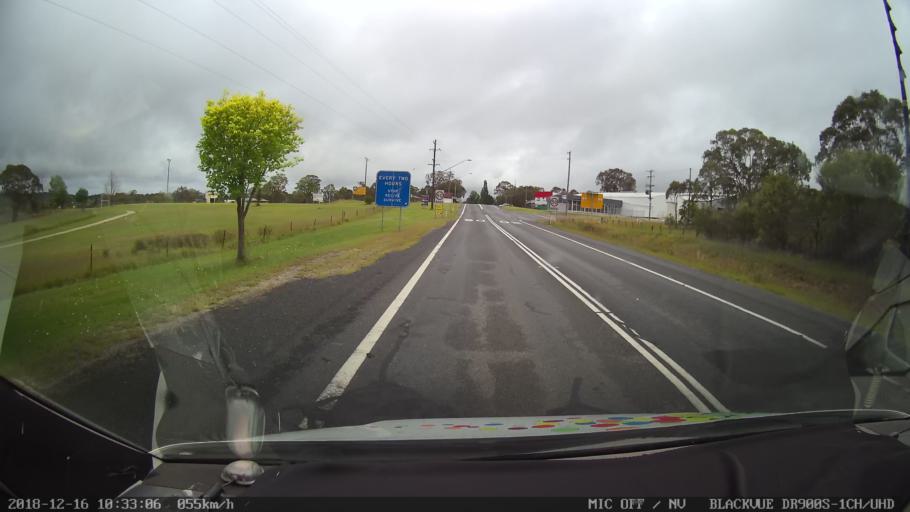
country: AU
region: New South Wales
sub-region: Tenterfield Municipality
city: Carrolls Creek
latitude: -29.0669
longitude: 152.0151
